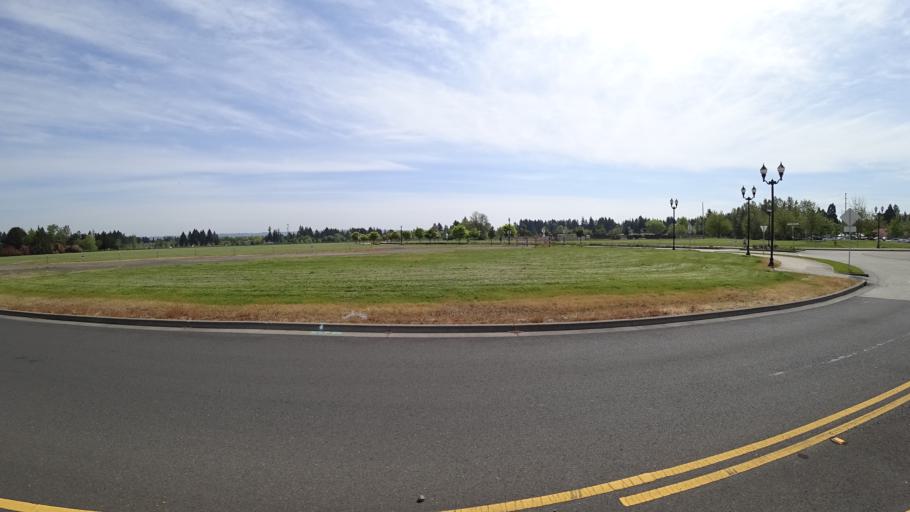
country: US
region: Oregon
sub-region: Washington County
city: Hillsboro
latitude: 45.5291
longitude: -122.9469
